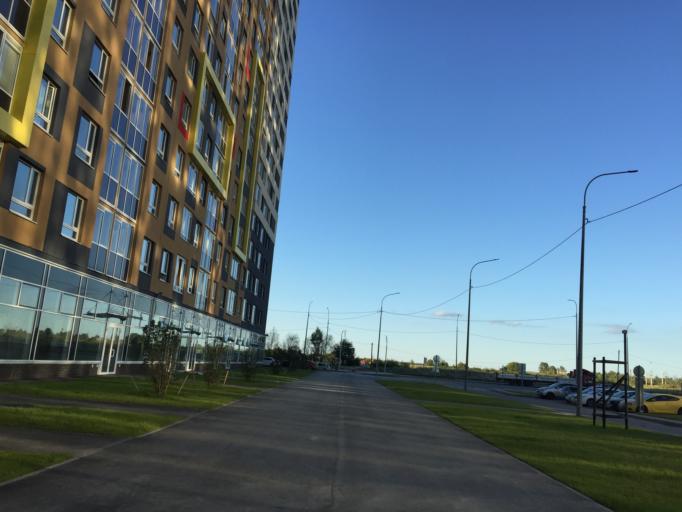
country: RU
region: Leningrad
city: Murino
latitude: 60.0678
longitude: 30.4284
